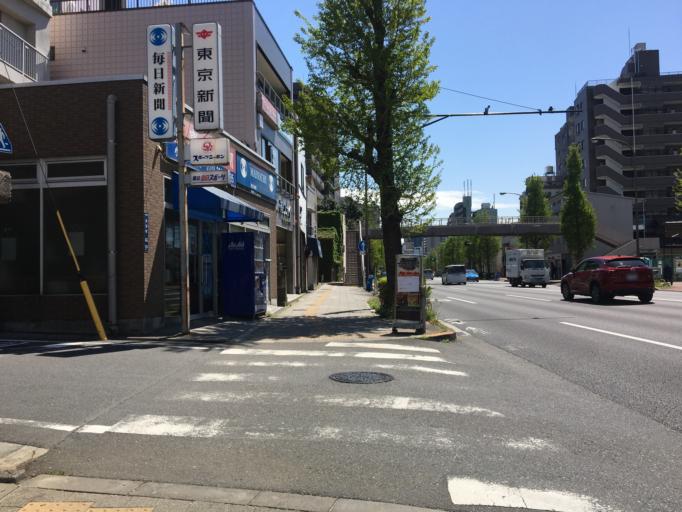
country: JP
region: Saitama
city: Kawaguchi
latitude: 35.7702
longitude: 139.7012
